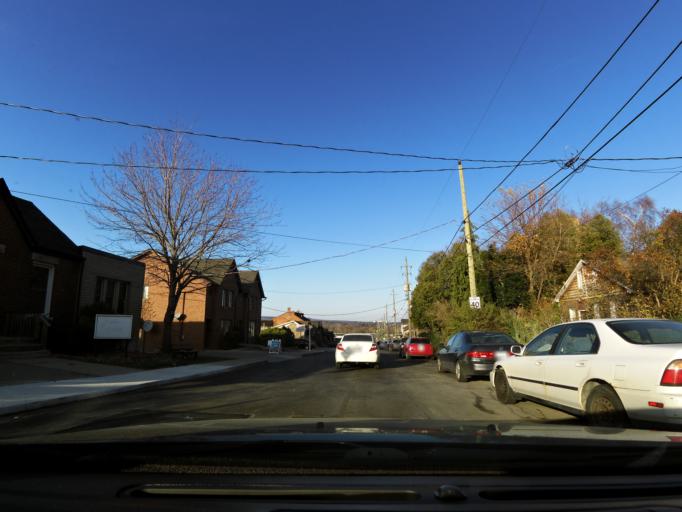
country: CA
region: Ontario
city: Hamilton
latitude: 43.2644
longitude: -79.8749
